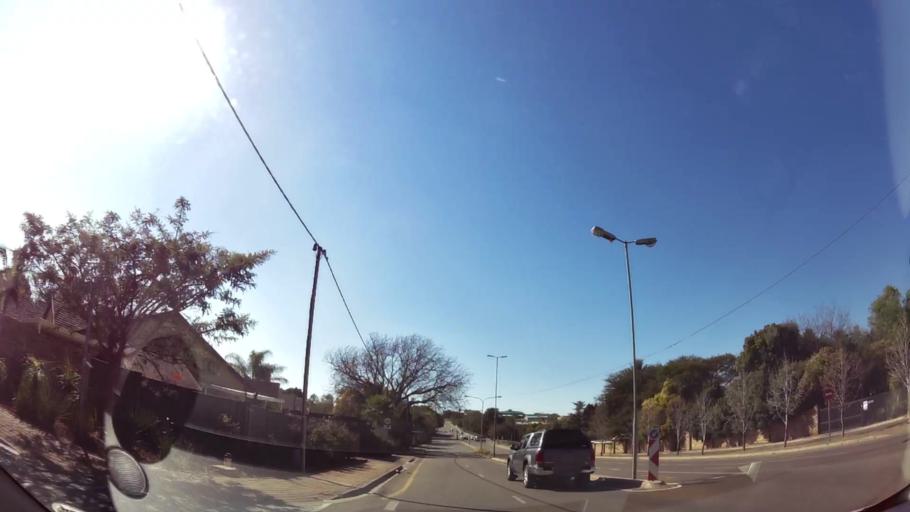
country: ZA
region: Gauteng
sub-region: City of Tshwane Metropolitan Municipality
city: Centurion
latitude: -25.8410
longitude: 28.2102
